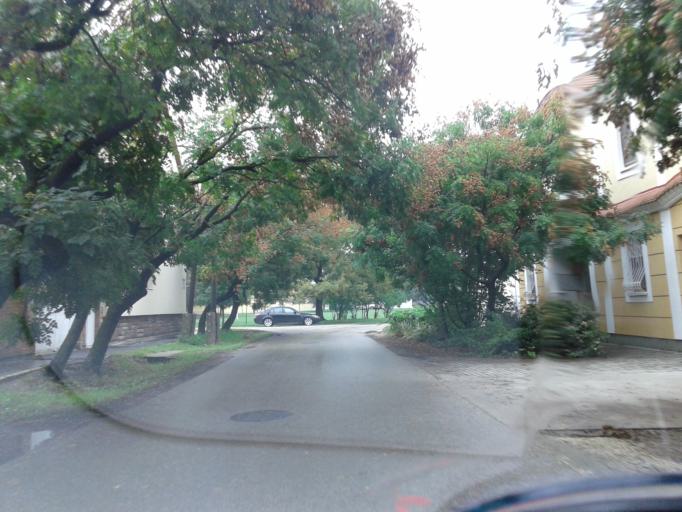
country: HU
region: Csongrad
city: Szeged
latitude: 46.2417
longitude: 20.1341
